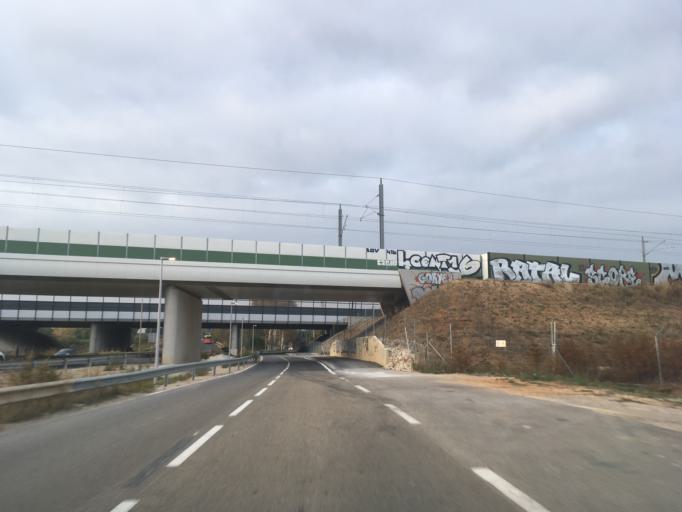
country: FR
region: Languedoc-Roussillon
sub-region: Departement de l'Herault
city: Lattes
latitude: 43.5828
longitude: 3.8980
